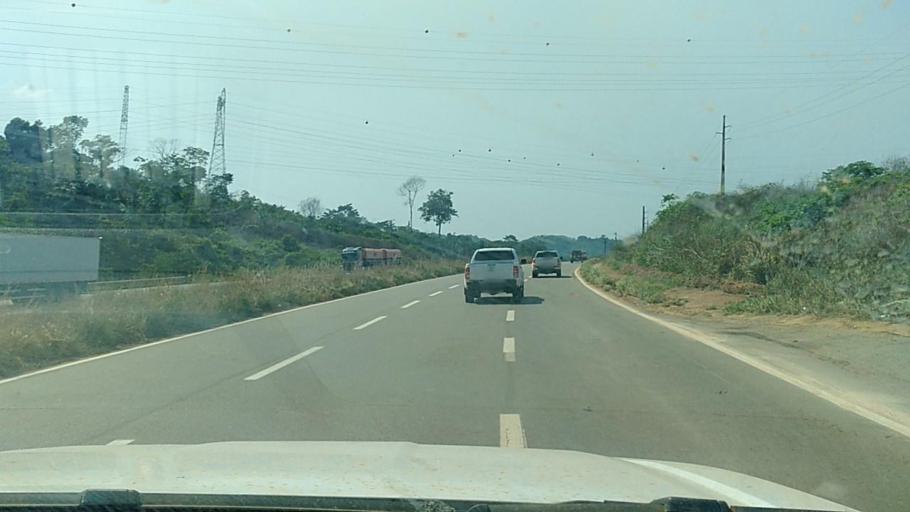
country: BR
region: Rondonia
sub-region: Porto Velho
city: Porto Velho
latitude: -8.7747
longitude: -63.4784
